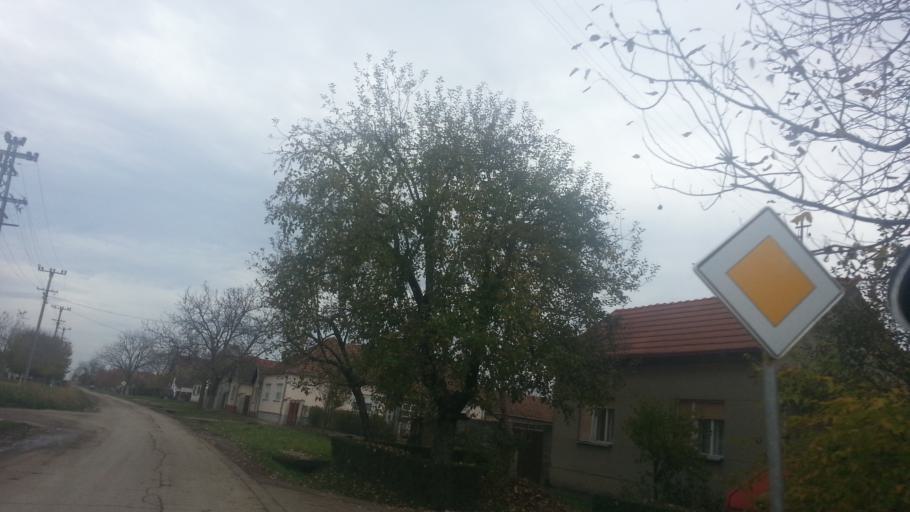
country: RS
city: Golubinci
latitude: 44.9928
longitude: 20.0665
